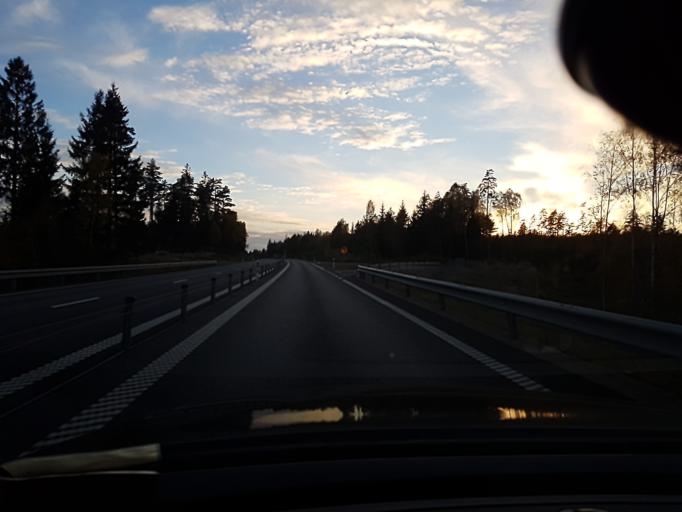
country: SE
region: Kronoberg
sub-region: Ljungby Kommun
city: Ljungby
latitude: 56.7854
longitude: 13.8268
